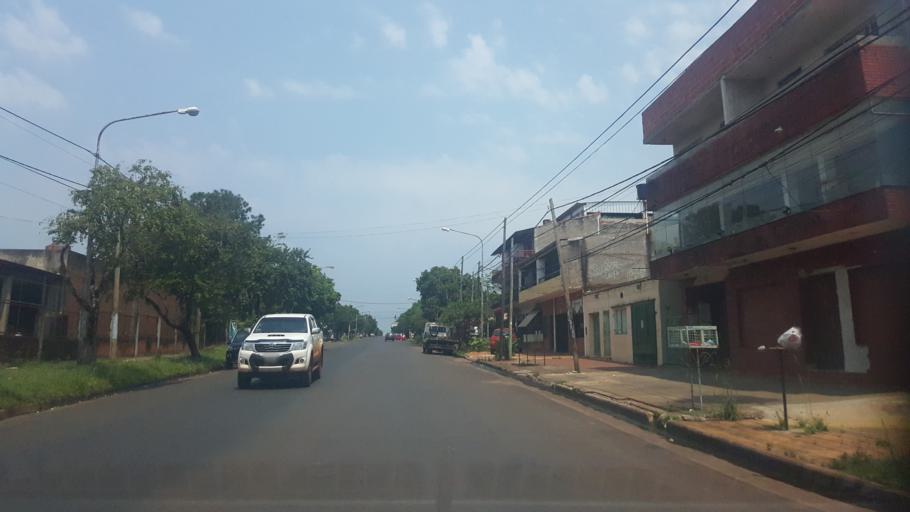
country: AR
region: Misiones
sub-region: Departamento de Capital
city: Posadas
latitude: -27.3819
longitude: -55.9072
